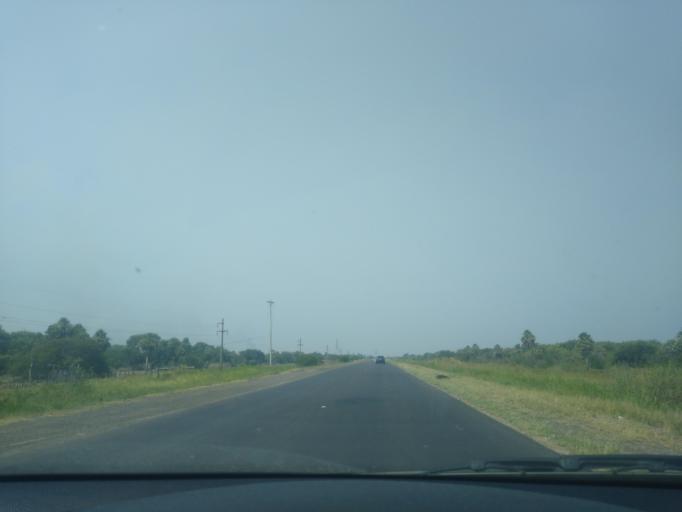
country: AR
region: Chaco
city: Fontana
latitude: -27.5005
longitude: -59.0844
